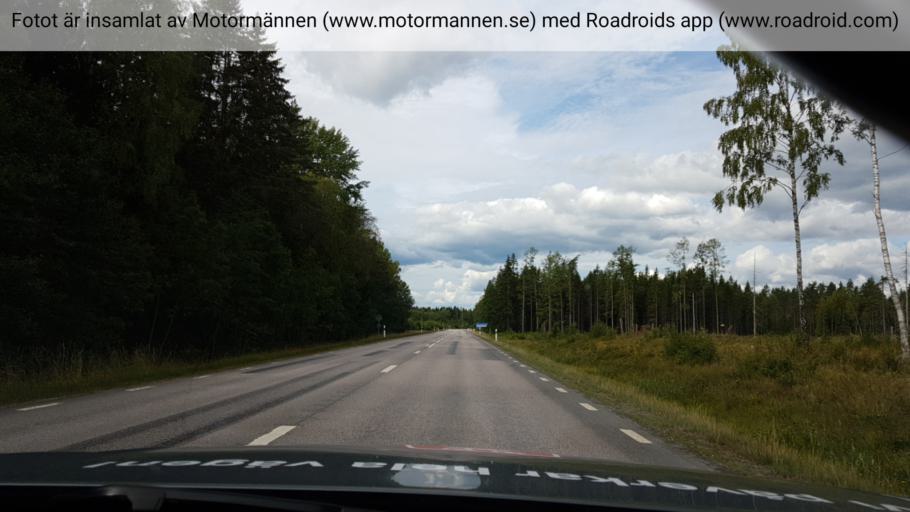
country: SE
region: Uppsala
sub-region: Heby Kommun
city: Morgongava
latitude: 59.8979
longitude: 17.0991
